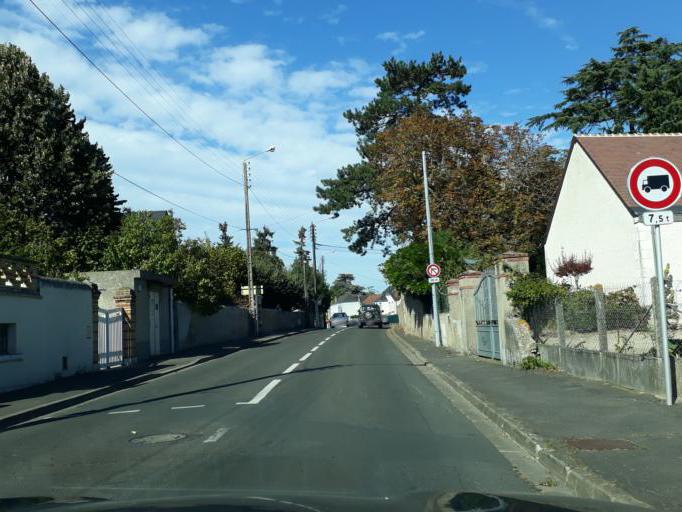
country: FR
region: Centre
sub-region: Departement d'Indre-et-Loire
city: Saint-Avertin
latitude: 47.3569
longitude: 0.7317
